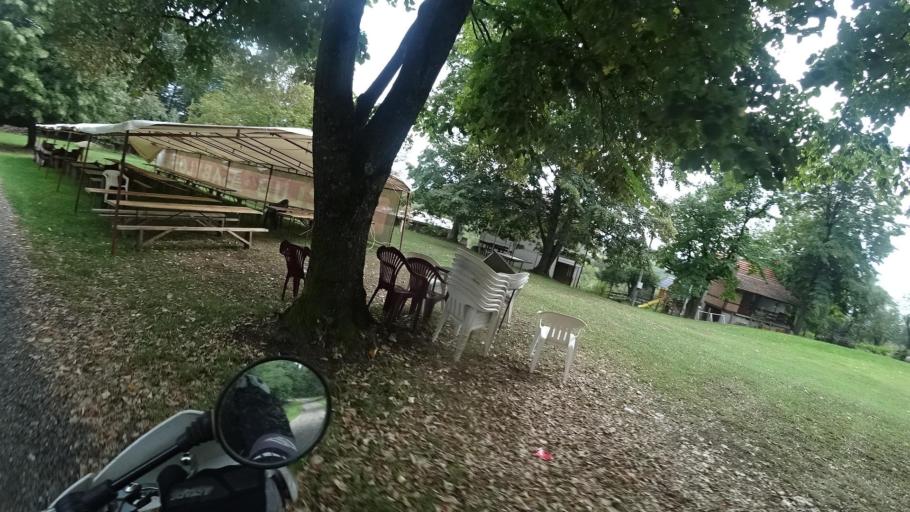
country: BA
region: Republika Srpska
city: Knezica
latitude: 45.0782
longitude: 16.6121
